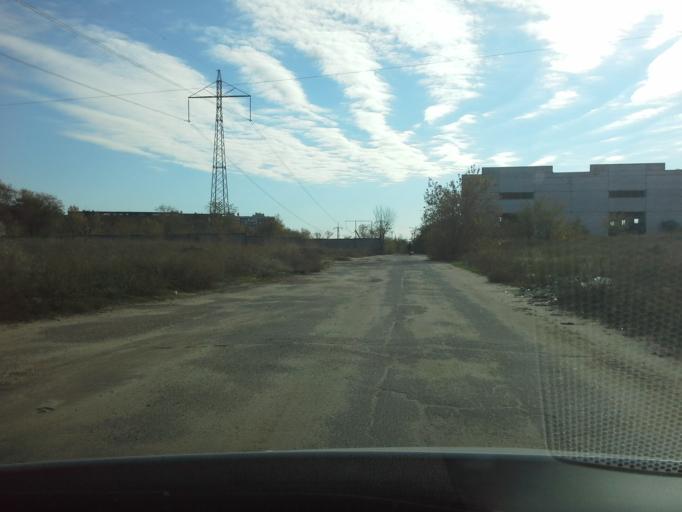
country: RU
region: Volgograd
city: Vodstroy
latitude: 48.8377
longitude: 44.6295
